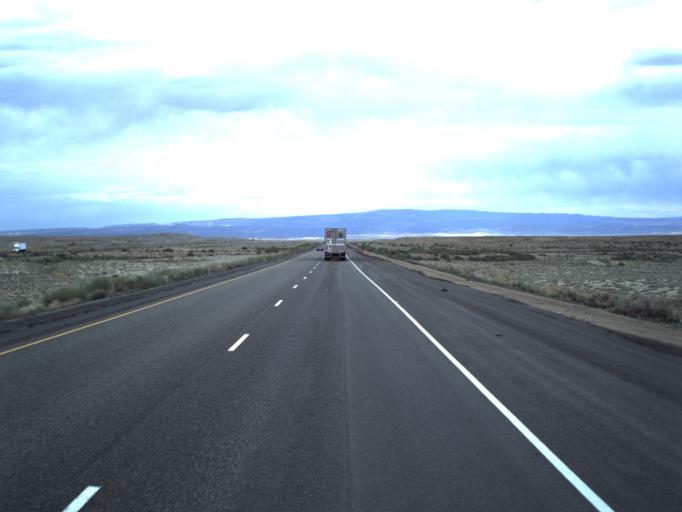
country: US
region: Utah
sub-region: Grand County
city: Moab
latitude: 38.9375
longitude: -109.4895
